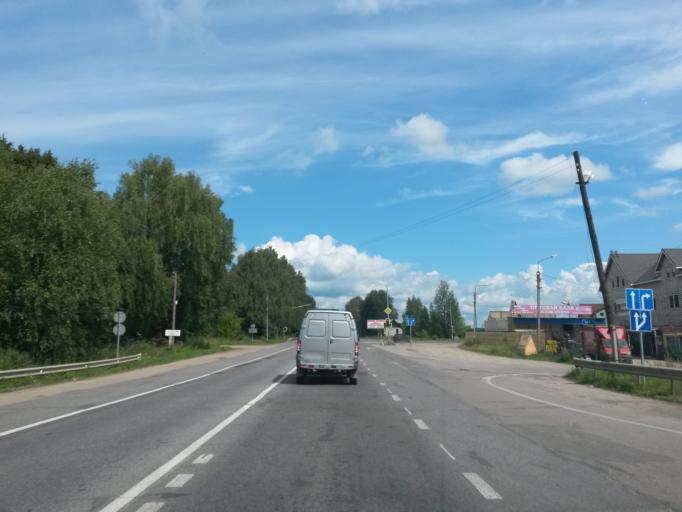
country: RU
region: Jaroslavl
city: Pereslavl'-Zalesskiy
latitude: 56.7809
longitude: 38.8816
